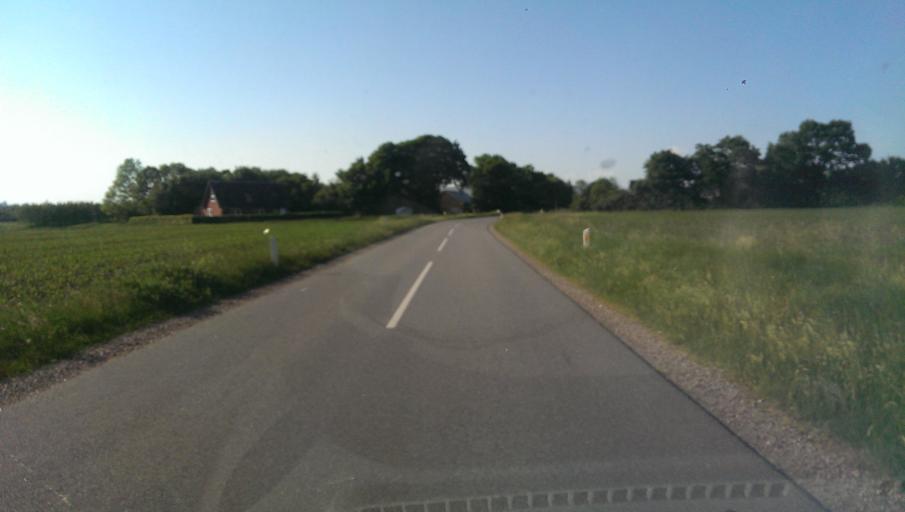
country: DK
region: South Denmark
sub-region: Esbjerg Kommune
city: Bramming
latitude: 55.5308
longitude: 8.6915
